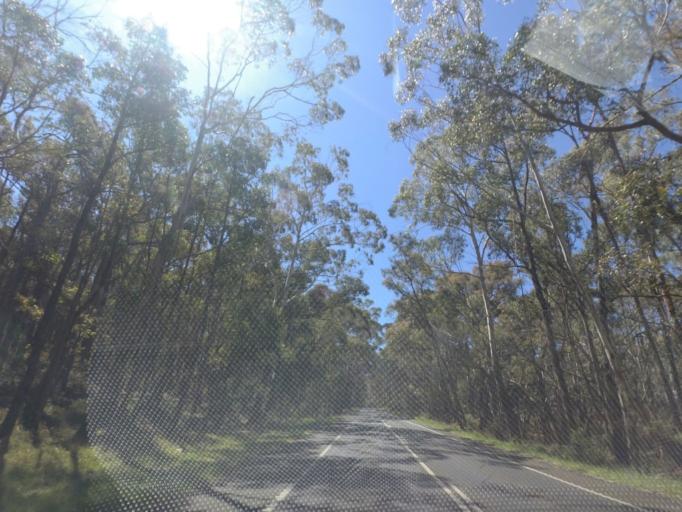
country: AU
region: Victoria
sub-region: Hume
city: Sunbury
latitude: -37.2292
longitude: 144.7410
